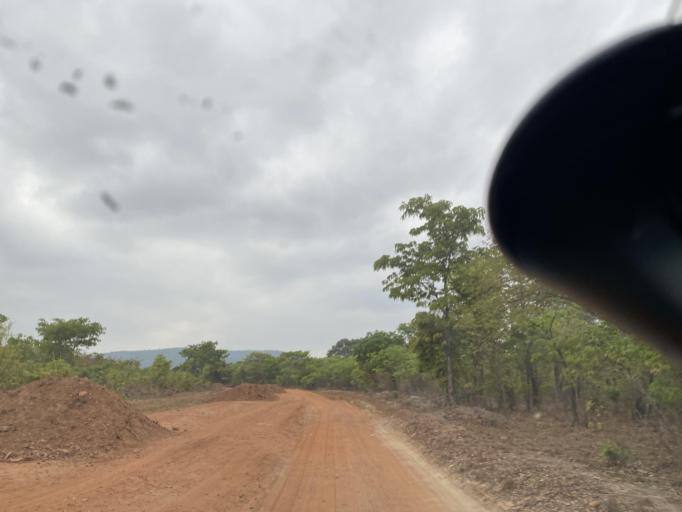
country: ZM
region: Lusaka
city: Chongwe
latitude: -15.2064
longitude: 28.7606
